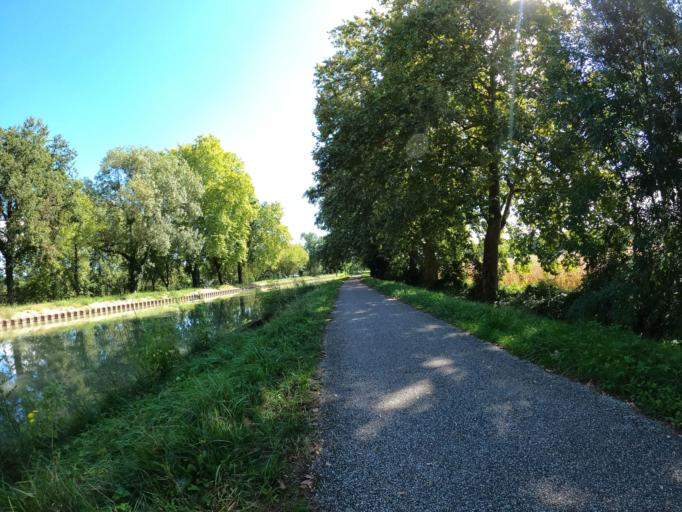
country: FR
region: Midi-Pyrenees
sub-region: Departement du Tarn-et-Garonne
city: Lamagistere
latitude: 44.1246
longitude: 0.8420
